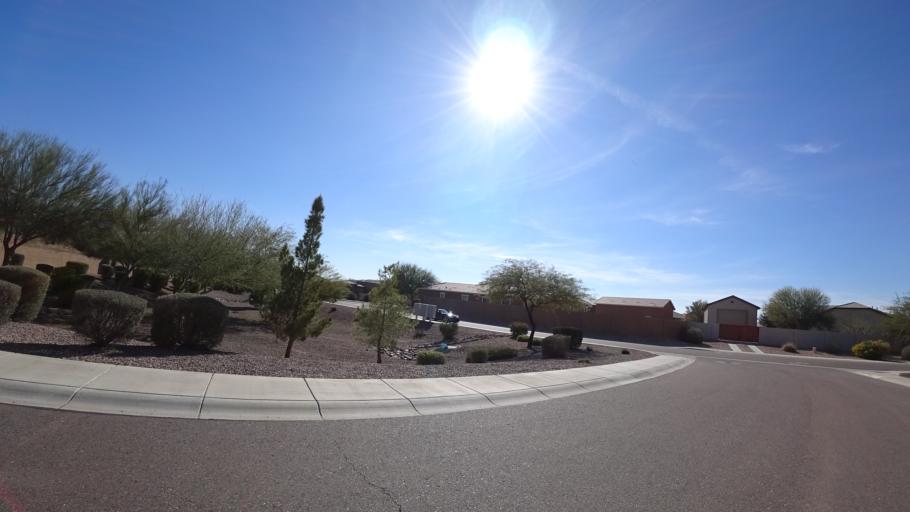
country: US
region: Arizona
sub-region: Maricopa County
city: Citrus Park
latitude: 33.5185
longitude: -112.4570
